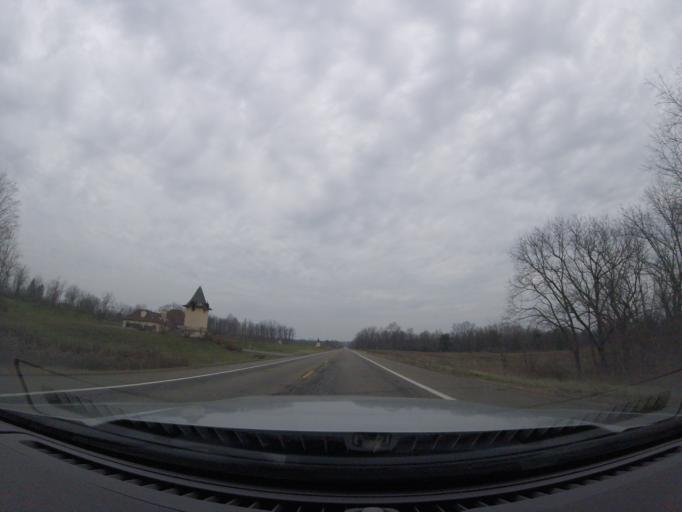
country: US
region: New York
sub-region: Yates County
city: Dundee
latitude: 42.4638
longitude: -76.9158
